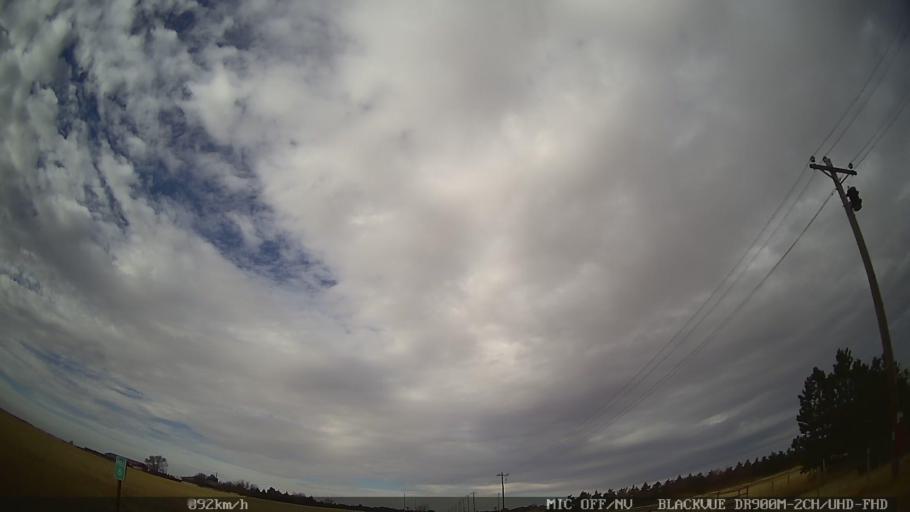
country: US
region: New Mexico
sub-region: Curry County
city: Texico
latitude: 34.4192
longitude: -103.0923
